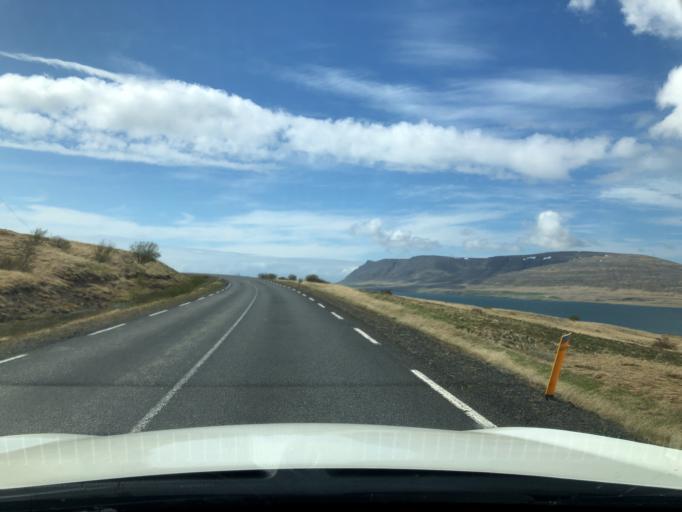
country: IS
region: Capital Region
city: Mosfellsbaer
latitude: 64.3319
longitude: -21.7340
